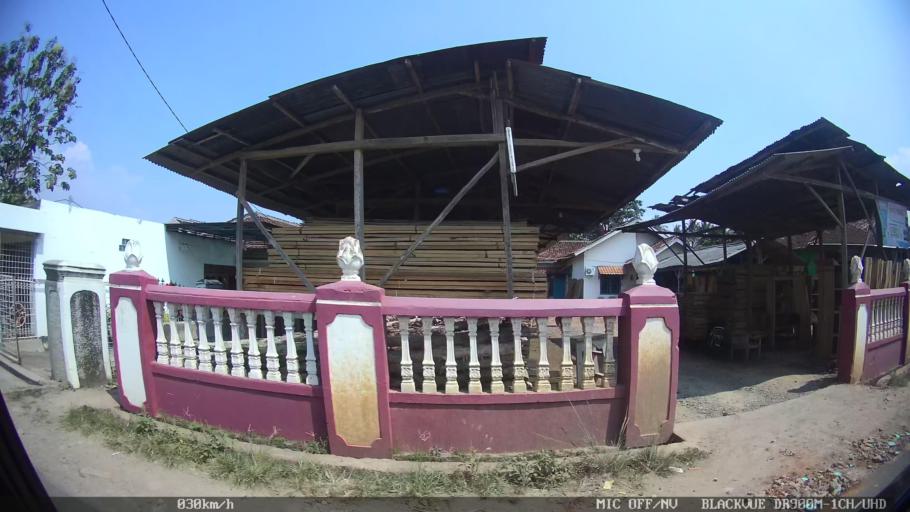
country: ID
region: Lampung
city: Natar
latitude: -5.3107
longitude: 105.2009
